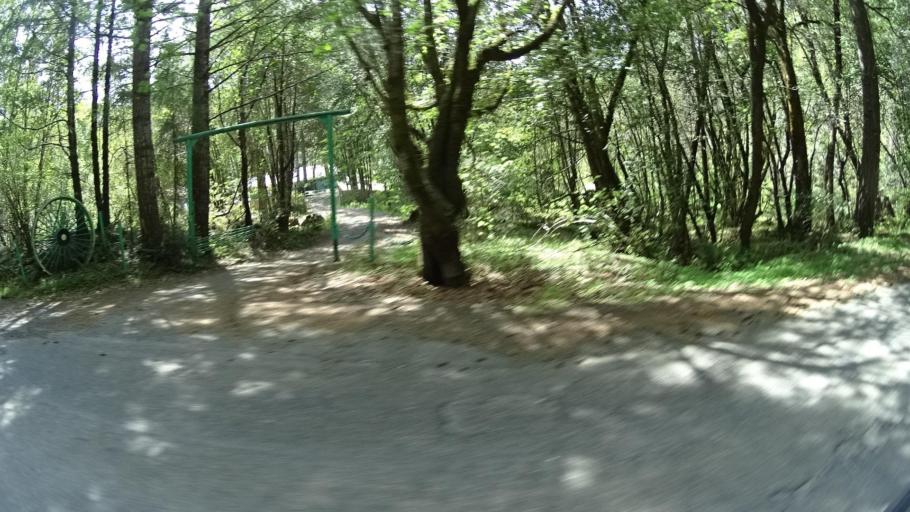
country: US
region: California
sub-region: Humboldt County
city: Redway
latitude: 40.3585
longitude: -123.7239
